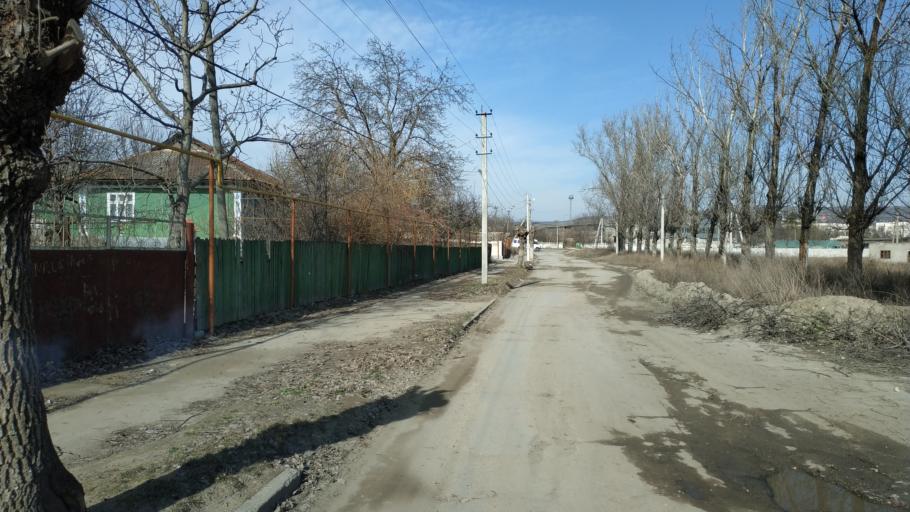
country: MD
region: Nisporeni
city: Nisporeni
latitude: 47.0710
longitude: 28.1751
